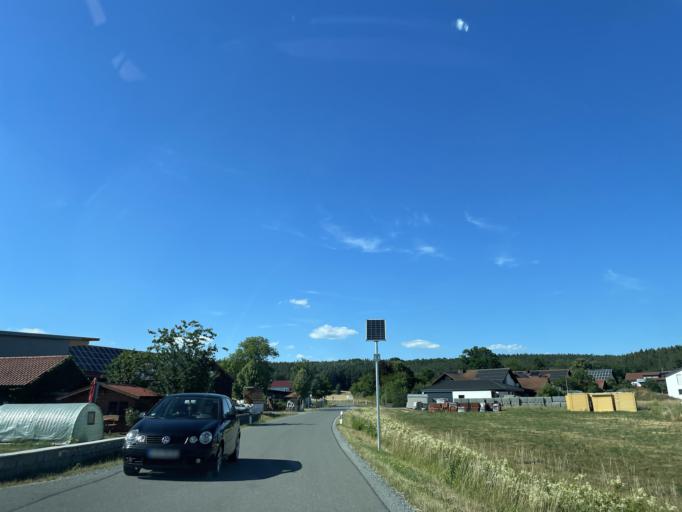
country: DE
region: Bavaria
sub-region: Upper Palatinate
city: Speinshart
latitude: 49.7733
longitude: 11.8603
